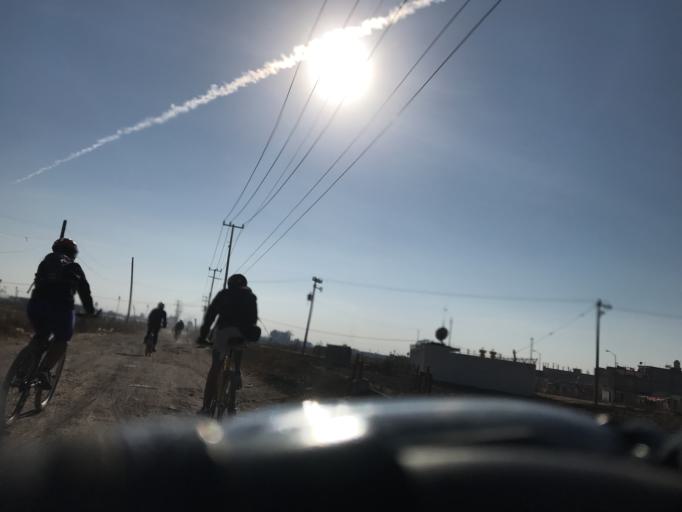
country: MX
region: Mexico
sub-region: Tonanitla
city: Colonia la Asuncion
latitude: 19.6962
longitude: -99.0720
